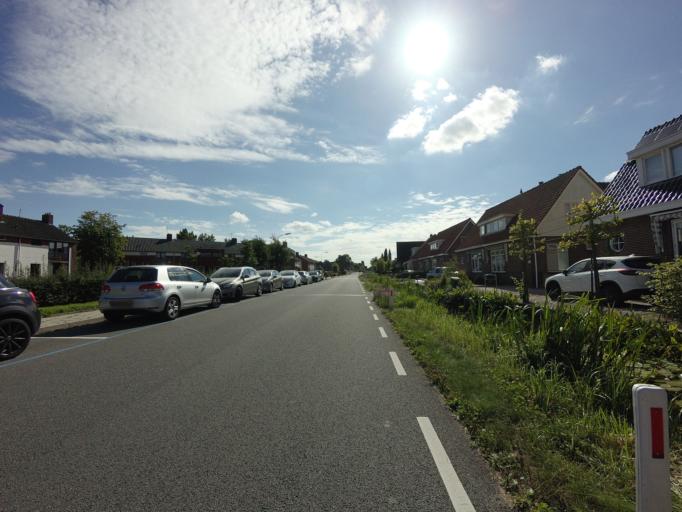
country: NL
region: Utrecht
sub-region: Gemeente De Ronde Venen
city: Mijdrecht
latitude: 52.2217
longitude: 4.9363
